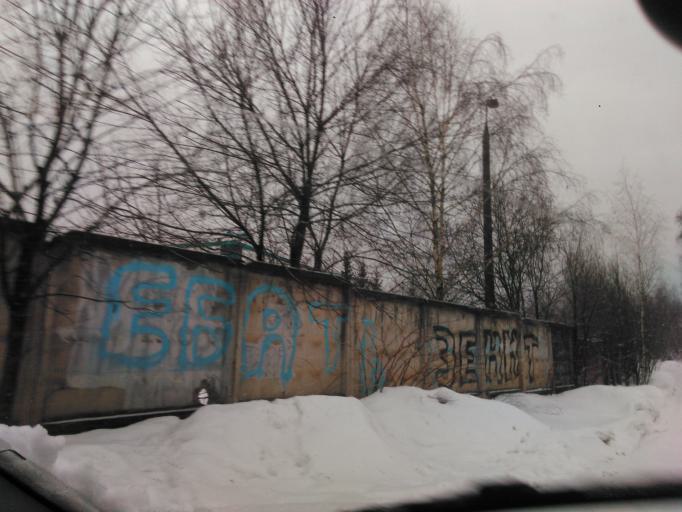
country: RU
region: Moskovskaya
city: Rzhavki
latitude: 56.0043
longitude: 37.2307
